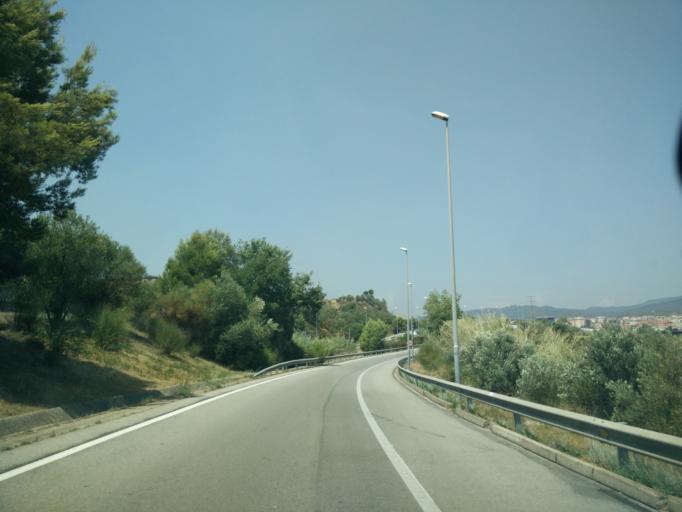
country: ES
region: Catalonia
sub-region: Provincia de Barcelona
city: Terrassa
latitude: 41.5431
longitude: 2.0165
